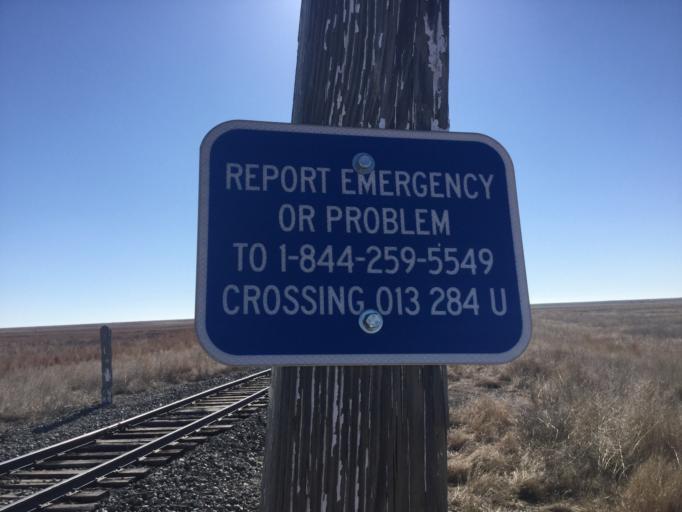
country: US
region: Kansas
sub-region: Haskell County
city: Satanta
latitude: 37.5163
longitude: -101.1443
